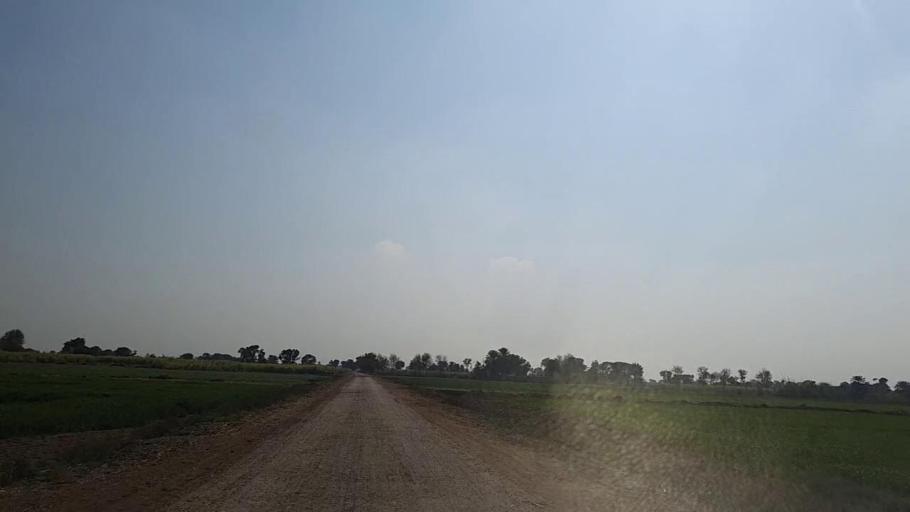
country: PK
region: Sindh
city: Daur
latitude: 26.4403
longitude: 68.2333
